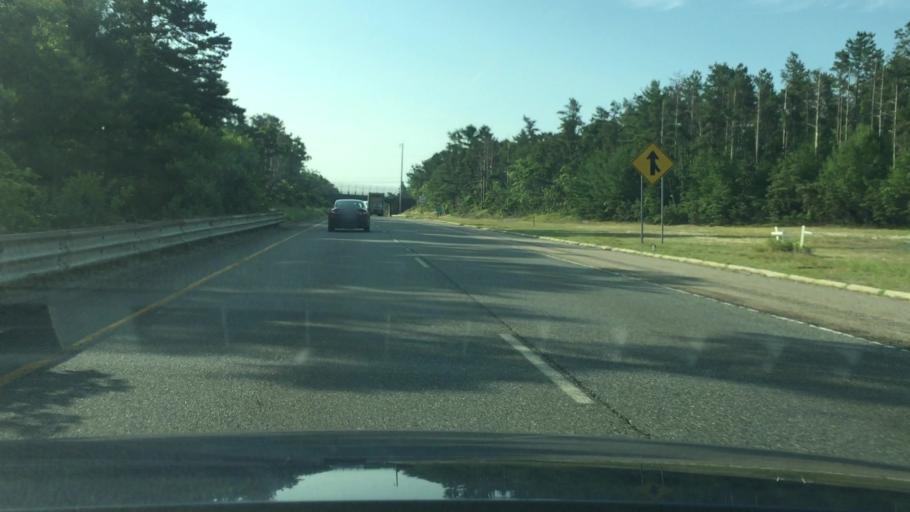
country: US
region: Massachusetts
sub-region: Plymouth County
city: White Island Shores
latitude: 41.8752
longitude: -70.6036
